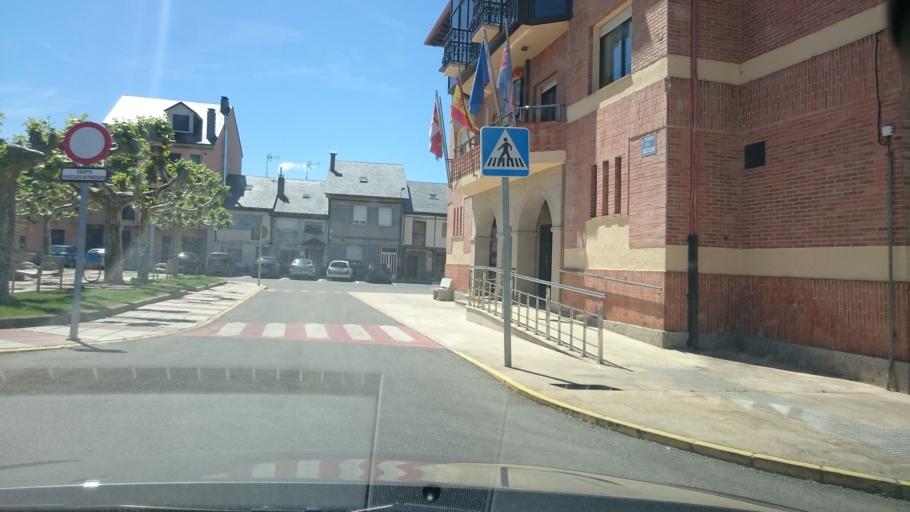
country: ES
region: Castille and Leon
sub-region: Provincia de Leon
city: Camponaraya
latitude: 42.5797
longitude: -6.6717
